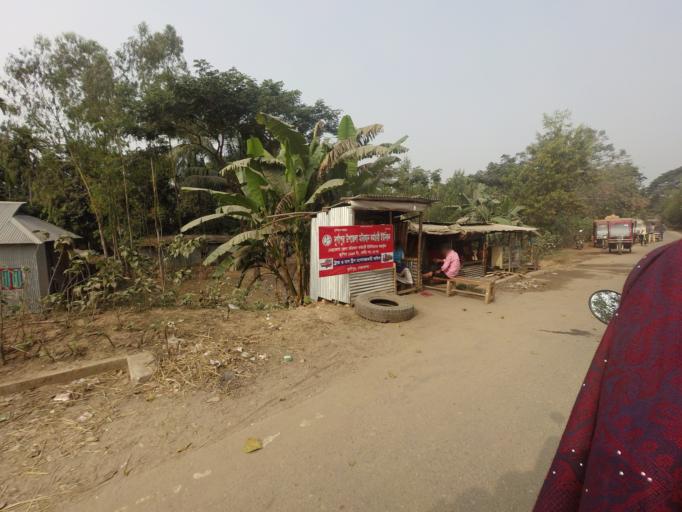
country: BD
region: Dhaka
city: Netrakona
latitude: 25.1195
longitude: 90.6653
